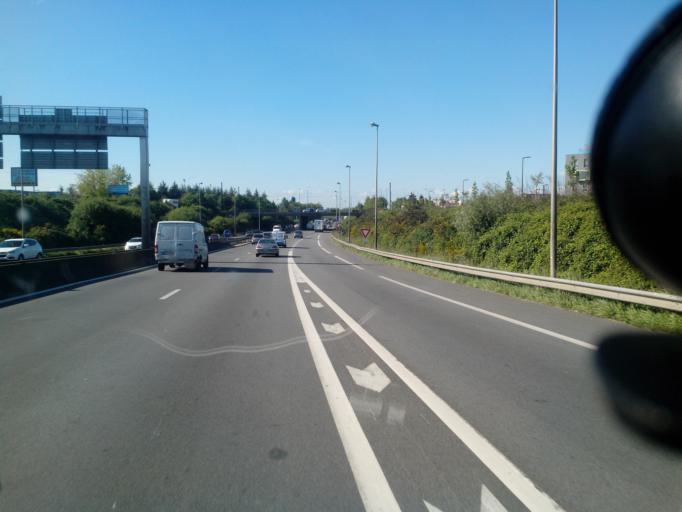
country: FR
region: Pays de la Loire
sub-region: Departement de la Loire-Atlantique
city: Saint-Herblain
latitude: 47.2216
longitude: -1.6222
